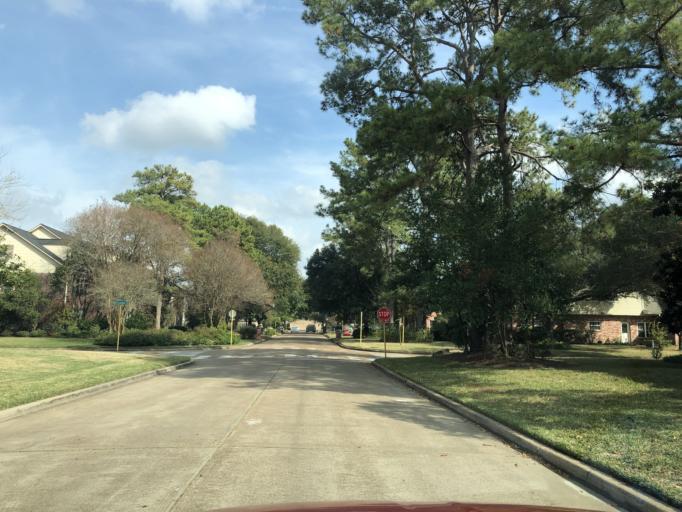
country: US
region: Texas
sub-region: Harris County
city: Tomball
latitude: 30.0231
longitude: -95.5428
